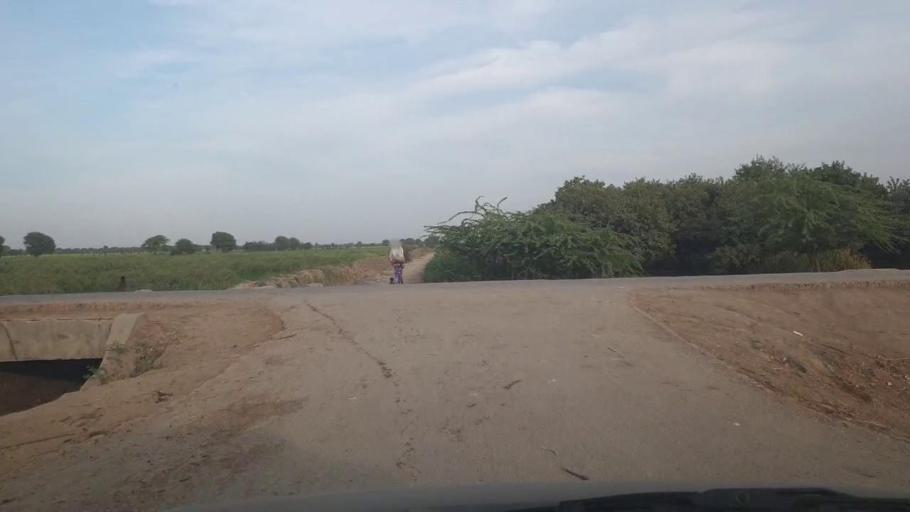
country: PK
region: Sindh
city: Kunri
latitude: 25.2647
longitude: 69.5452
